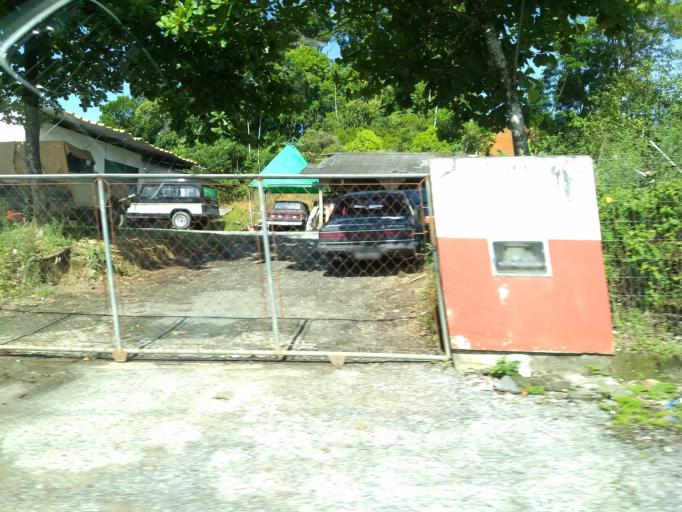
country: BR
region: Santa Catarina
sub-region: Schroeder
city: Schroeder
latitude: -26.4488
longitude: -49.1075
